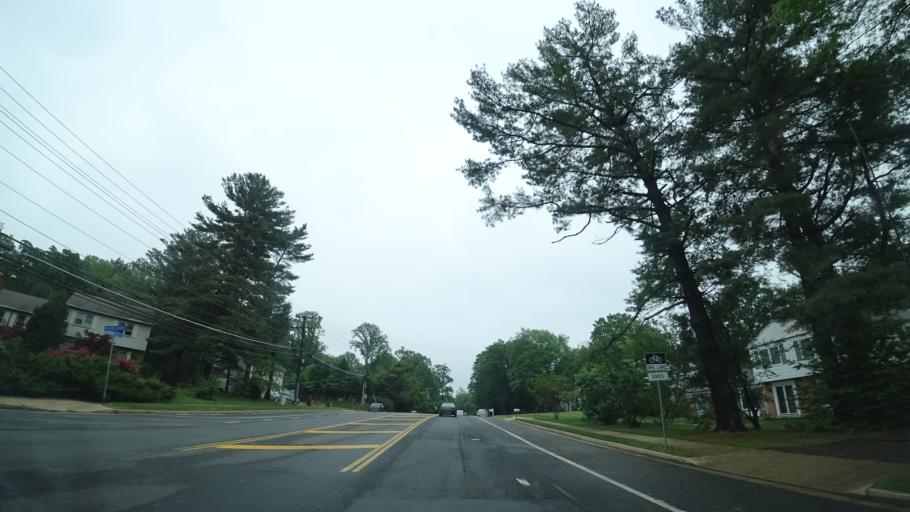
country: US
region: Virginia
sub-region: Fairfax County
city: Tysons Corner
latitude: 38.9417
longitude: -77.2212
